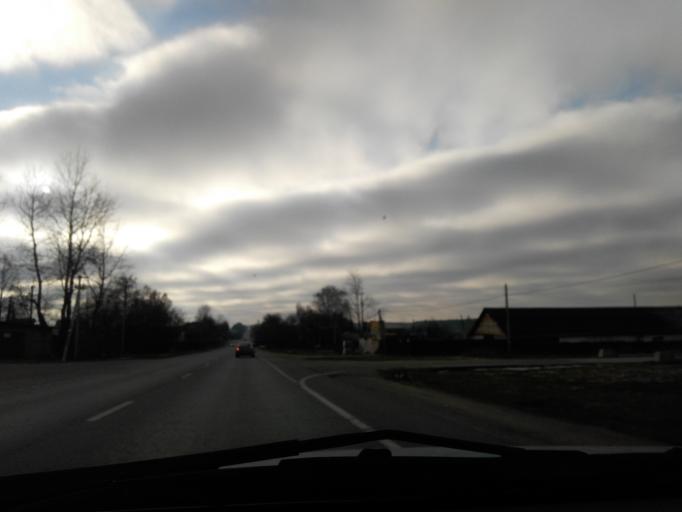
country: RU
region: Moskovskaya
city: Troitsk
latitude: 55.3087
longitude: 37.1468
